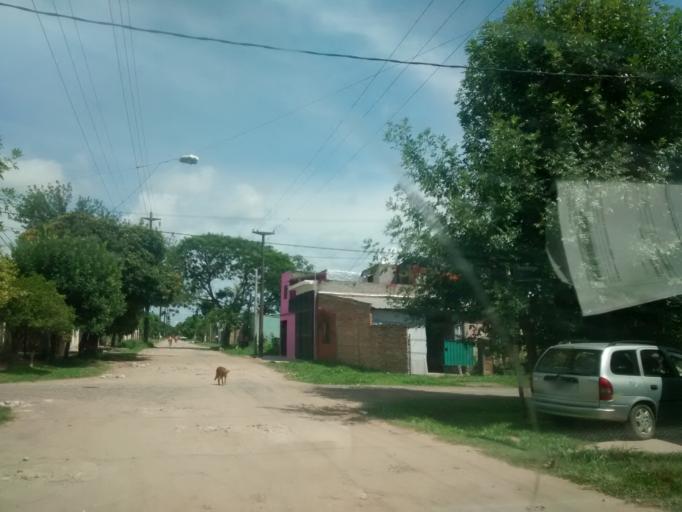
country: AR
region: Chaco
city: Resistencia
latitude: -27.4231
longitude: -58.9771
